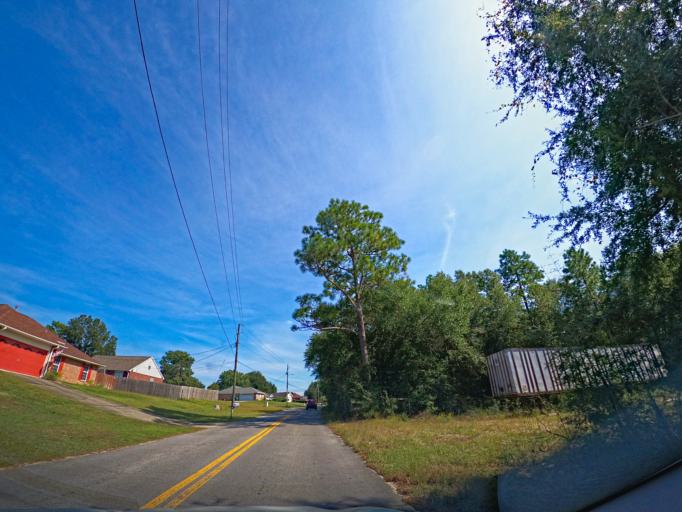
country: US
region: Florida
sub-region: Okaloosa County
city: Crestview
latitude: 30.7053
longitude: -86.5925
